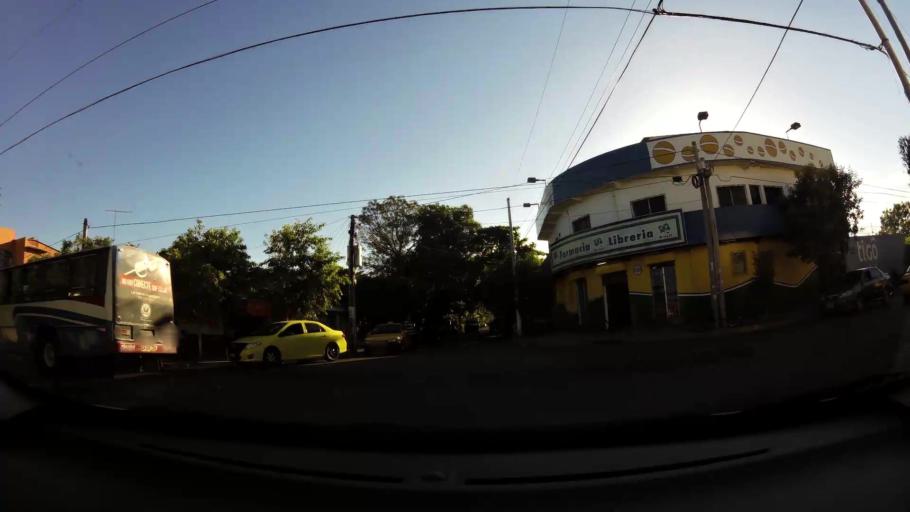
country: SV
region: San Miguel
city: San Miguel
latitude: 13.4876
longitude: -88.1692
